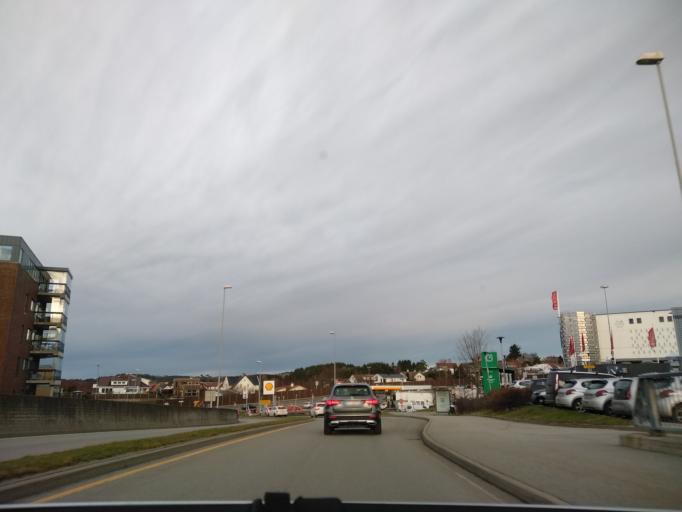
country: NO
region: Rogaland
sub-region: Stavanger
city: Stavanger
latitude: 58.9514
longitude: 5.6753
